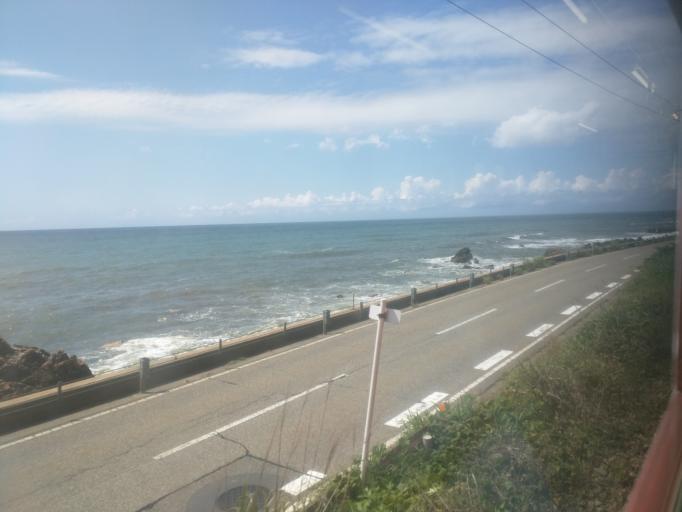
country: JP
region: Niigata
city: Murakami
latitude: 38.4580
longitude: 139.4976
